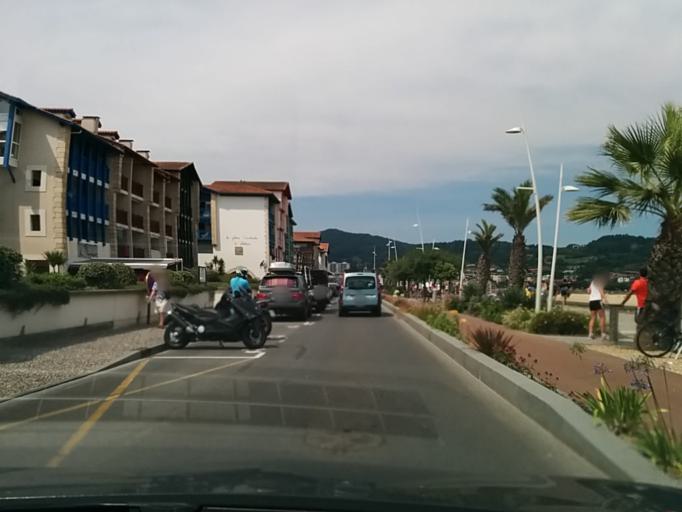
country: FR
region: Aquitaine
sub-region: Departement des Pyrenees-Atlantiques
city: Hendaye
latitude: 43.3720
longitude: -1.7831
